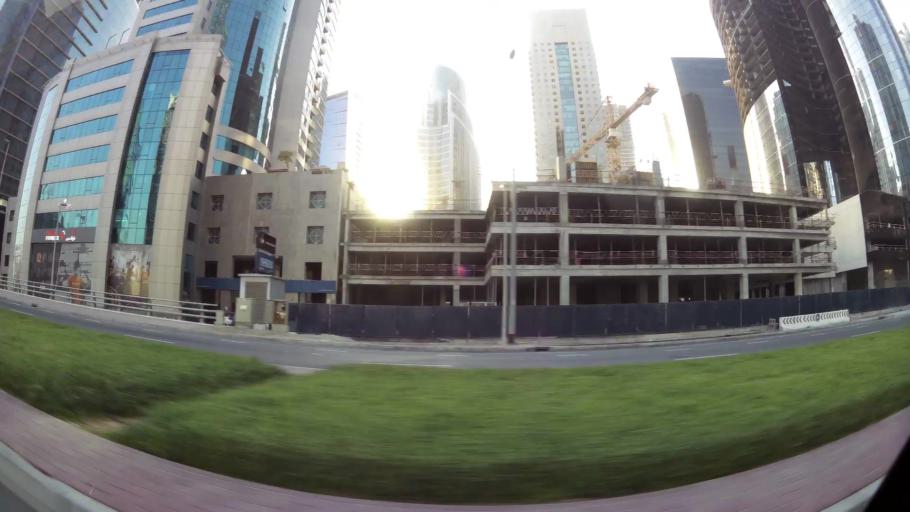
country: AE
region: Dubai
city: Dubai
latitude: 25.1862
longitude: 55.2629
